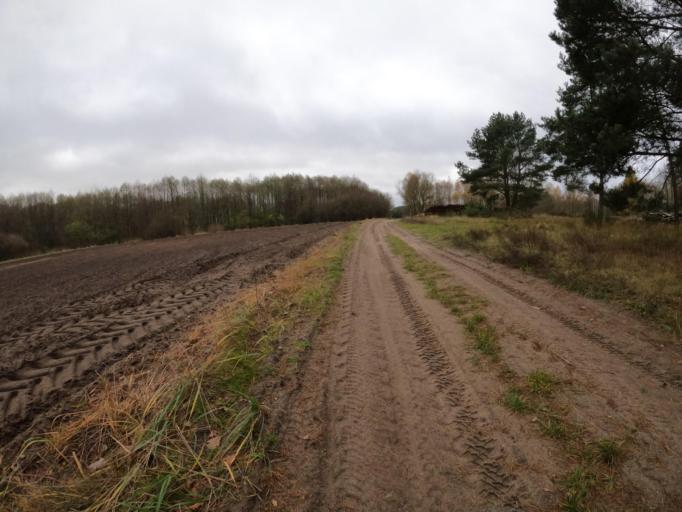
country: PL
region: West Pomeranian Voivodeship
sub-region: Powiat walecki
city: Tuczno
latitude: 53.2802
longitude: 16.1503
